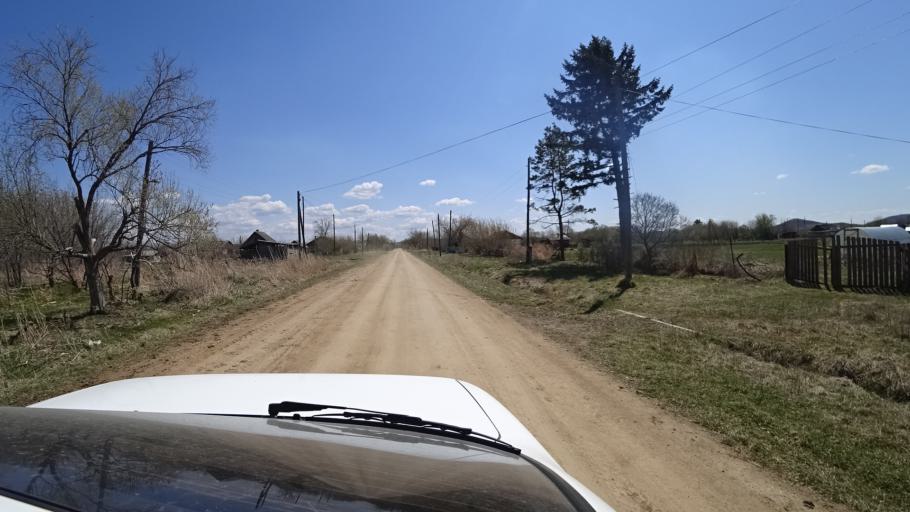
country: RU
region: Primorskiy
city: Dal'nerechensk
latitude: 45.8025
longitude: 133.7649
